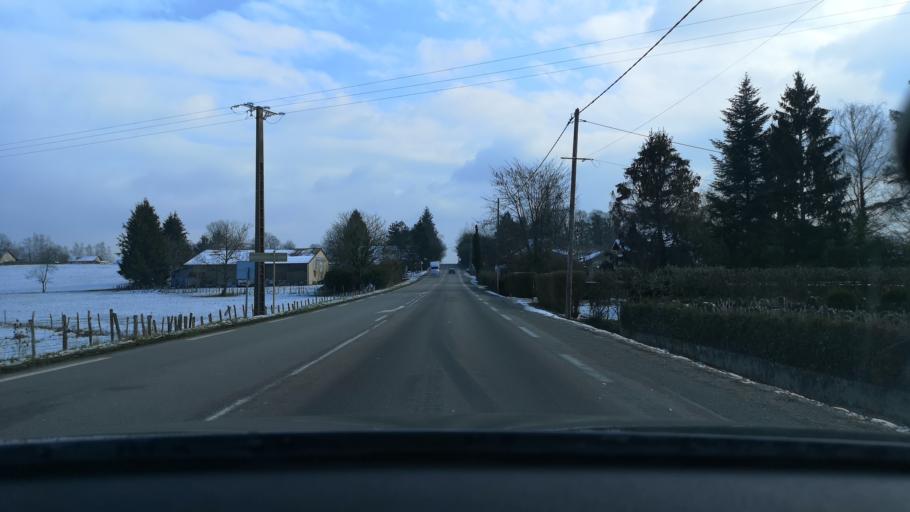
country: FR
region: Franche-Comte
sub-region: Departement du Jura
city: Bletterans
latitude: 46.6713
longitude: 5.3946
